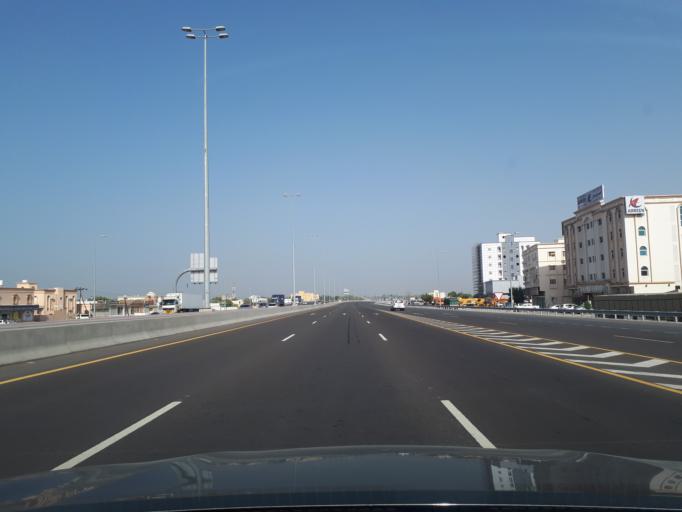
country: OM
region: Al Batinah
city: Al Liwa'
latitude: 24.4208
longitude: 56.6194
